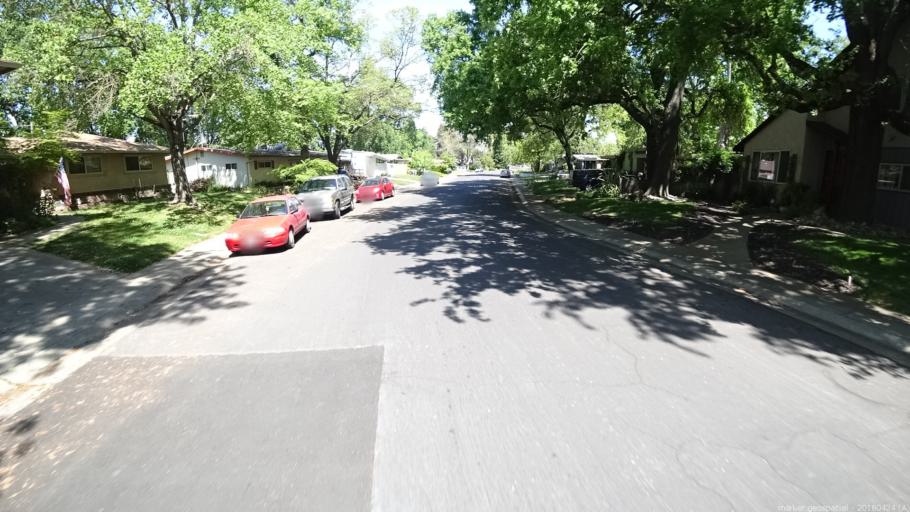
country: US
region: California
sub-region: Yolo County
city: West Sacramento
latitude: 38.5675
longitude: -121.5368
